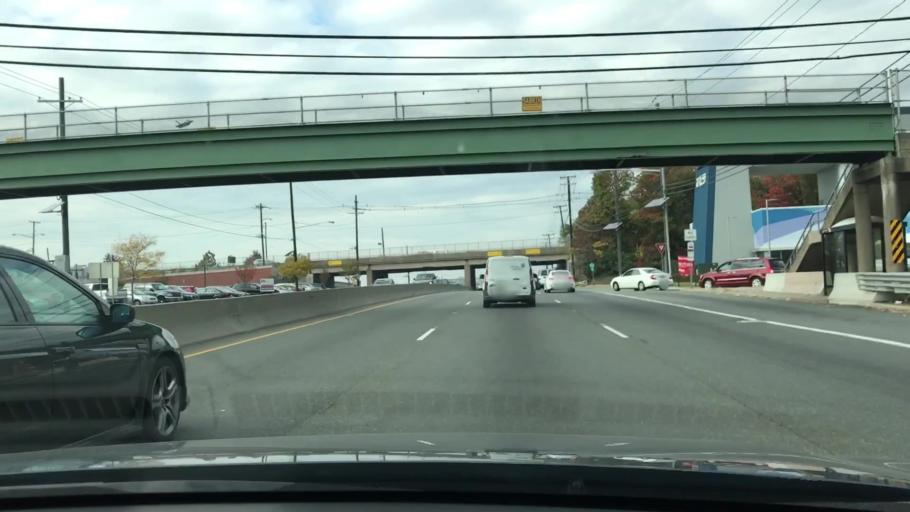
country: US
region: New Jersey
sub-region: Bergen County
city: Maywood
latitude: 40.9158
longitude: -74.0532
